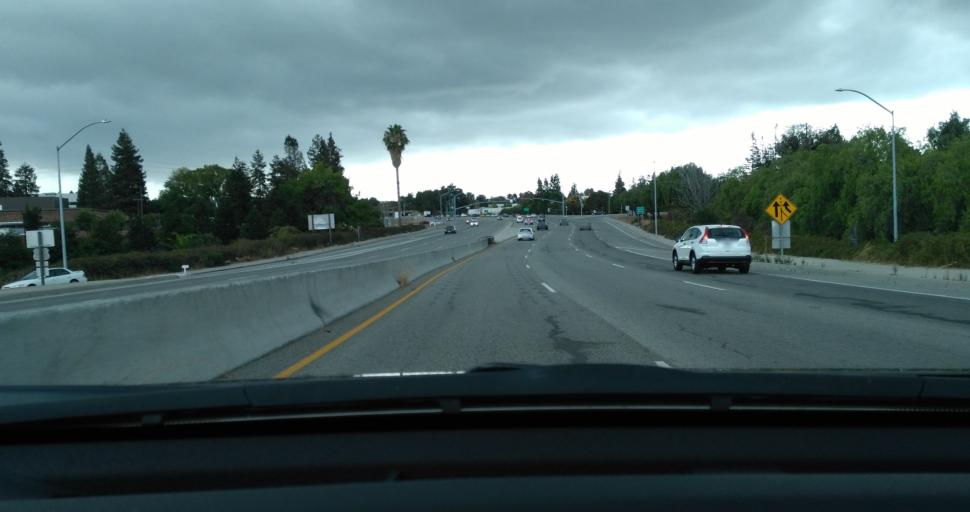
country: US
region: California
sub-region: Santa Clara County
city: Santa Clara
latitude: 37.3809
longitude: -121.9645
